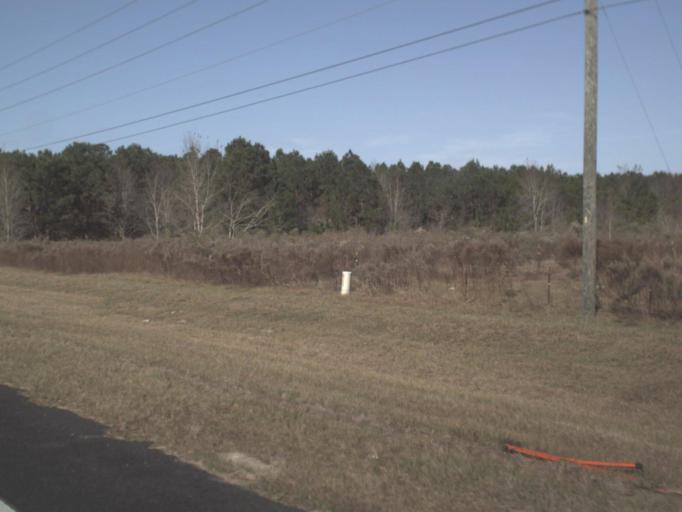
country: US
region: Florida
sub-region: Marion County
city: Belleview
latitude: 29.0259
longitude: -82.1260
